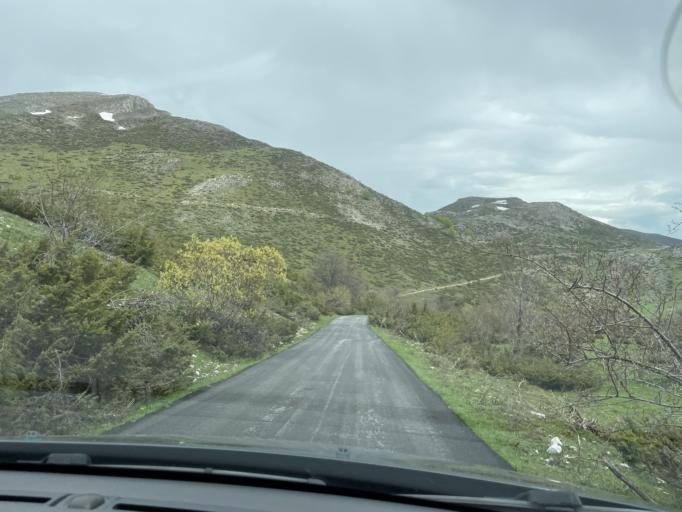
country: MK
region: Opstina Rostusa
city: Rostusha
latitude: 41.6247
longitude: 20.6823
